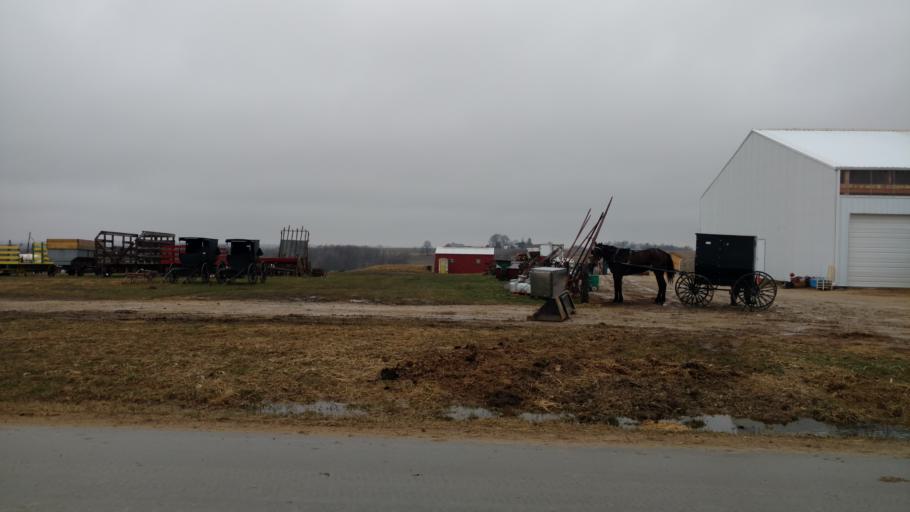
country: US
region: Wisconsin
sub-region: Monroe County
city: Cashton
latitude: 43.7147
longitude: -90.7145
